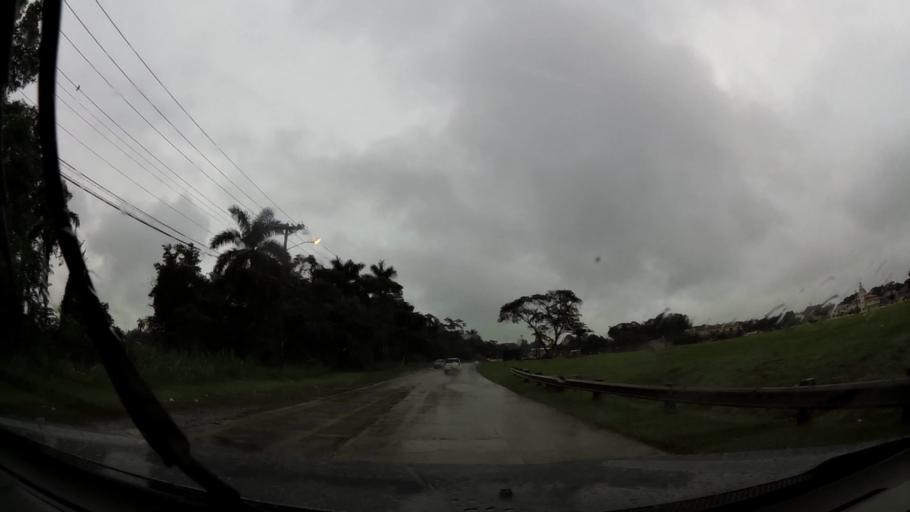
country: PA
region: Colon
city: Las Margaritas
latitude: 9.3227
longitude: -79.8967
